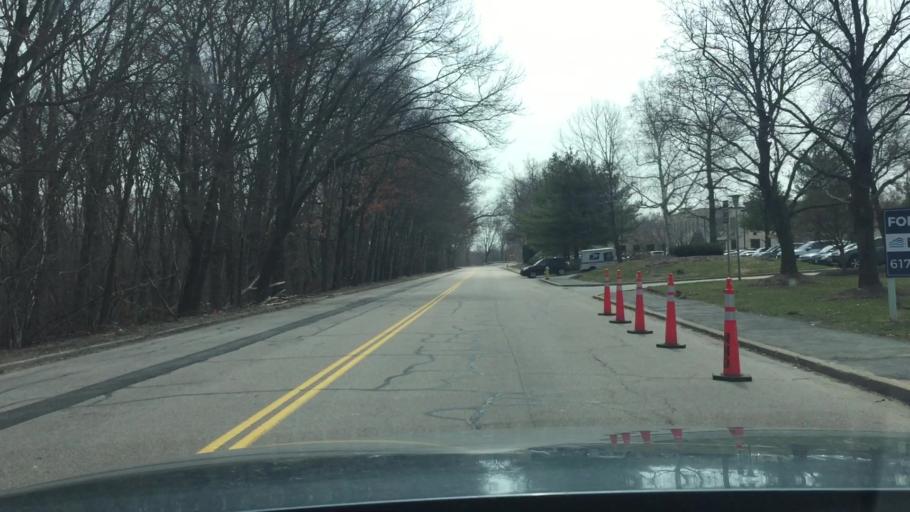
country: US
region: Massachusetts
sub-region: Norfolk County
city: Needham
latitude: 42.2990
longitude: -71.2119
